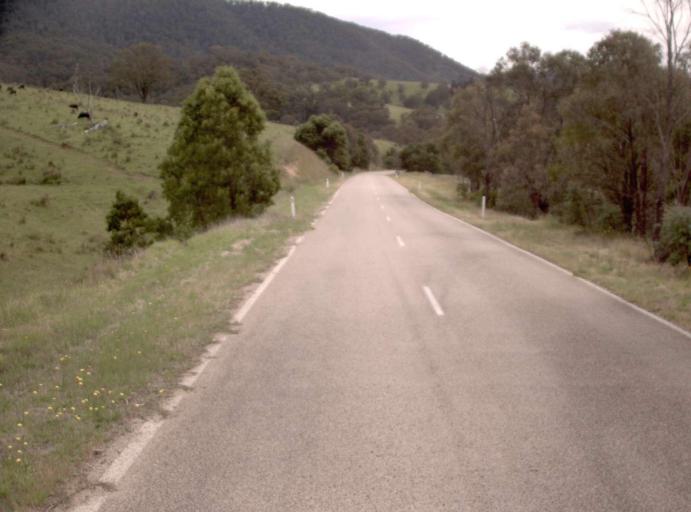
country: AU
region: Victoria
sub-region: East Gippsland
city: Bairnsdale
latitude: -37.5863
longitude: 147.1838
